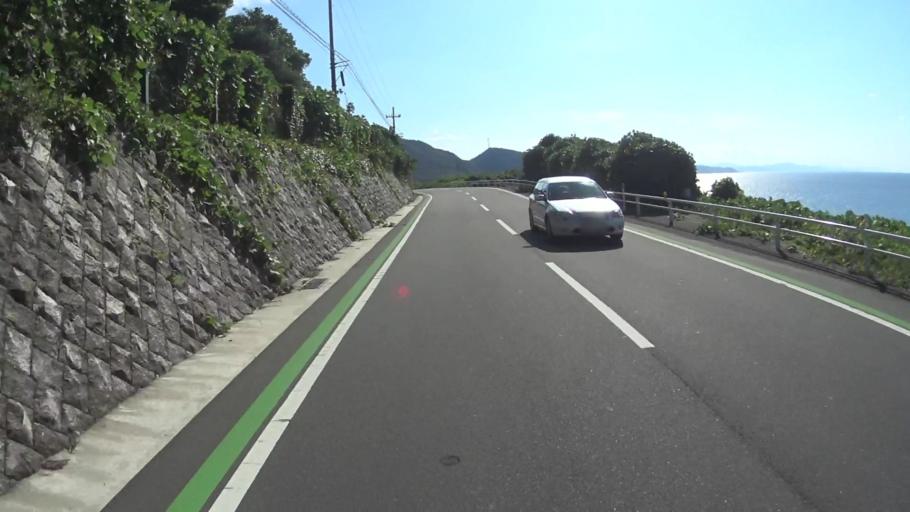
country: JP
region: Kyoto
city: Miyazu
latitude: 35.7275
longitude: 135.0869
